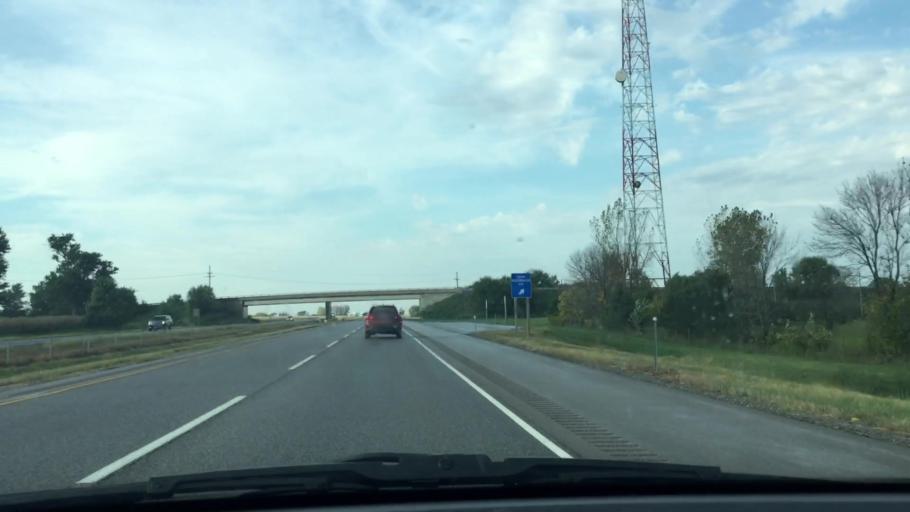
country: US
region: Illinois
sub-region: Lee County
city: Dixon
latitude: 41.7890
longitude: -89.5333
